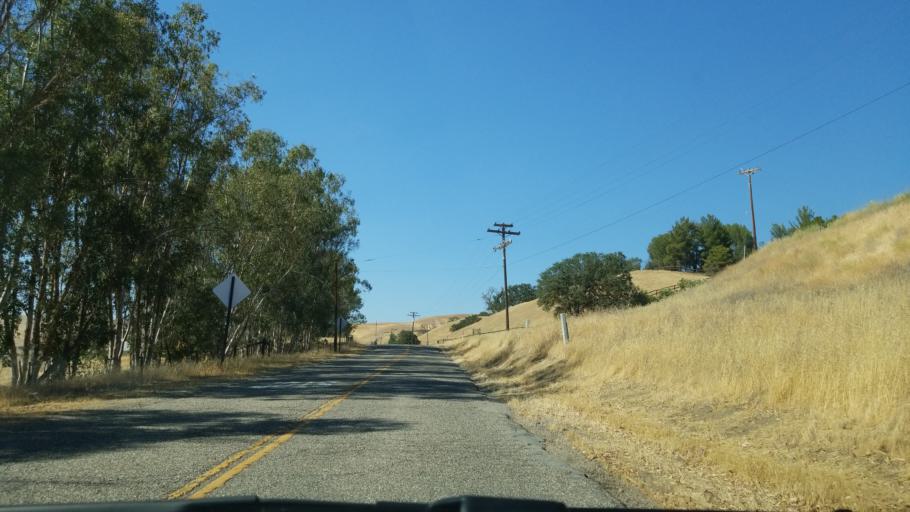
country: US
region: California
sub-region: San Luis Obispo County
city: San Miguel
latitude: 35.7564
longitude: -120.6852
